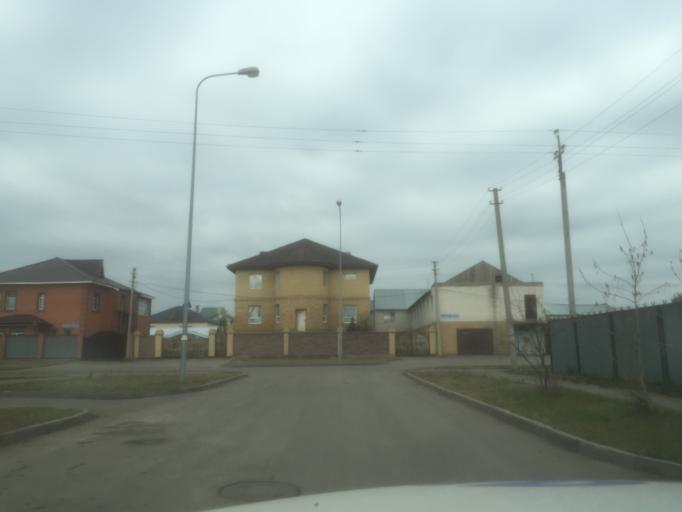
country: KZ
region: Astana Qalasy
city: Astana
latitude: 51.1757
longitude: 71.3742
